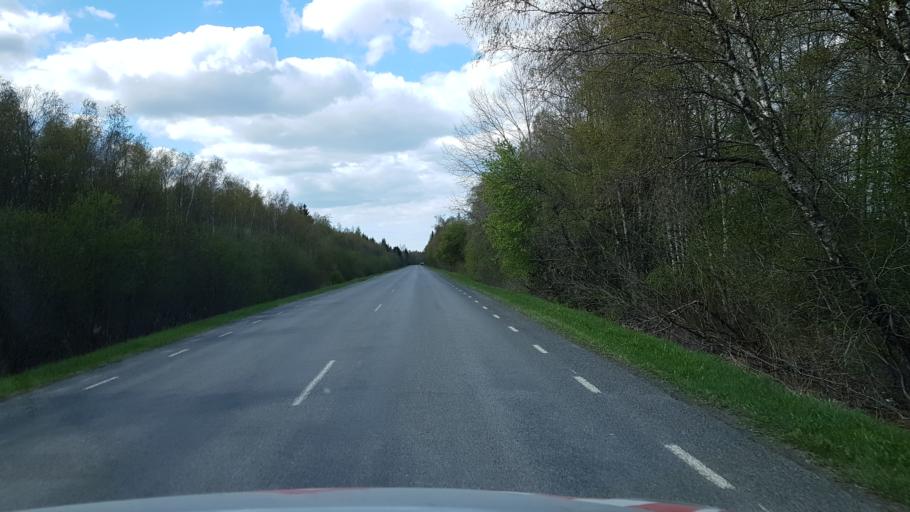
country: EE
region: Harju
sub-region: Keila linn
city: Keila
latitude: 59.2939
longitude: 24.4380
